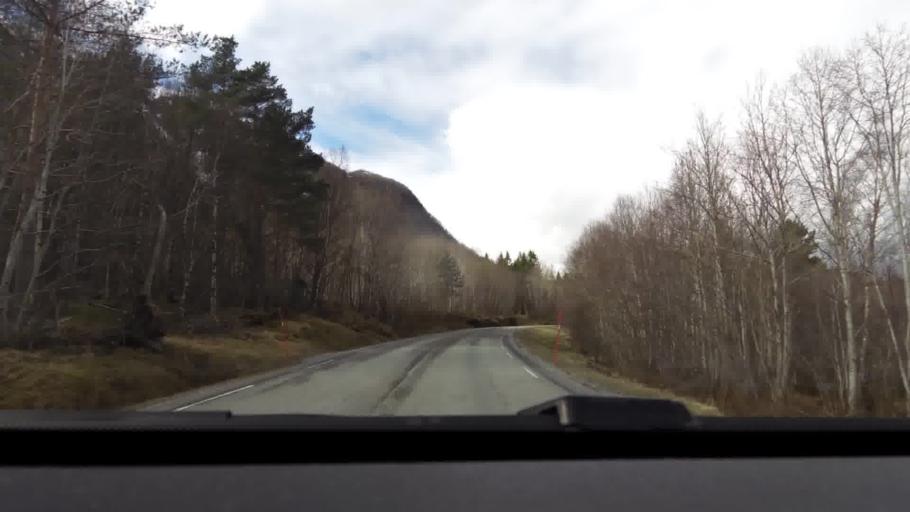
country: NO
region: More og Romsdal
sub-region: Averoy
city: Bruhagen
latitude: 63.1009
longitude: 7.6271
